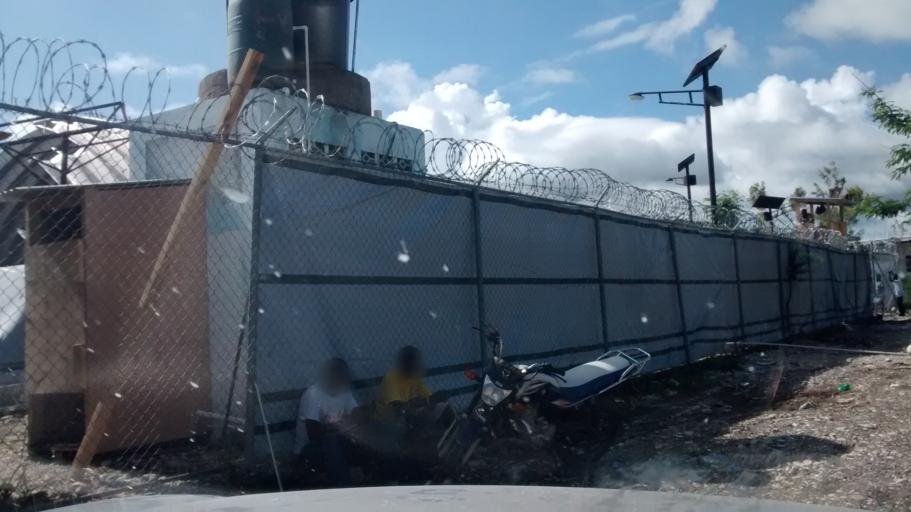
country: HT
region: Grandans
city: Jeremie
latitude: 18.6210
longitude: -74.0925
